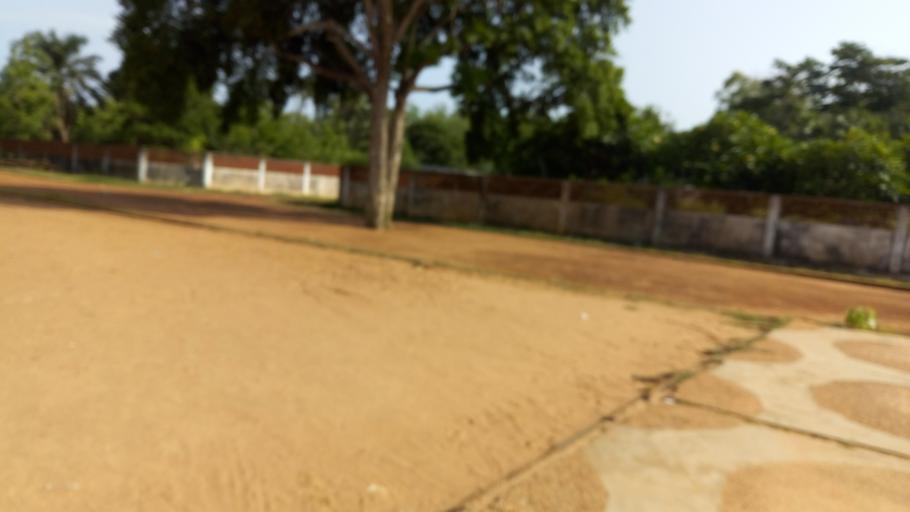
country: TG
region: Maritime
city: Lome
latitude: 6.1913
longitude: 1.1621
